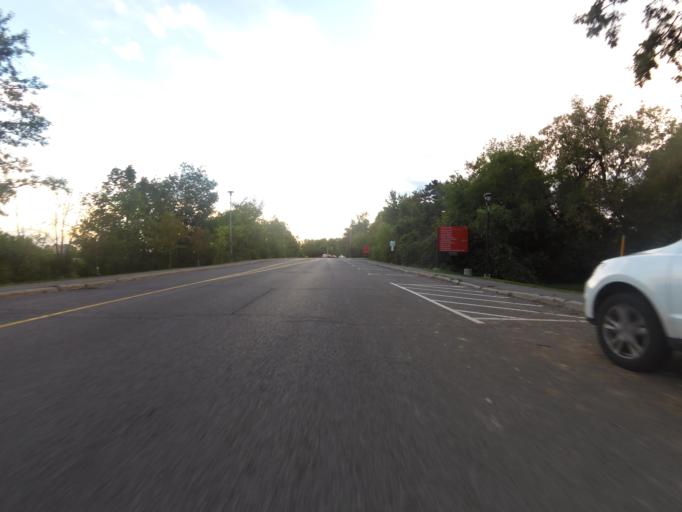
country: CA
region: Ontario
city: Ottawa
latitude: 45.3798
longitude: -75.6997
